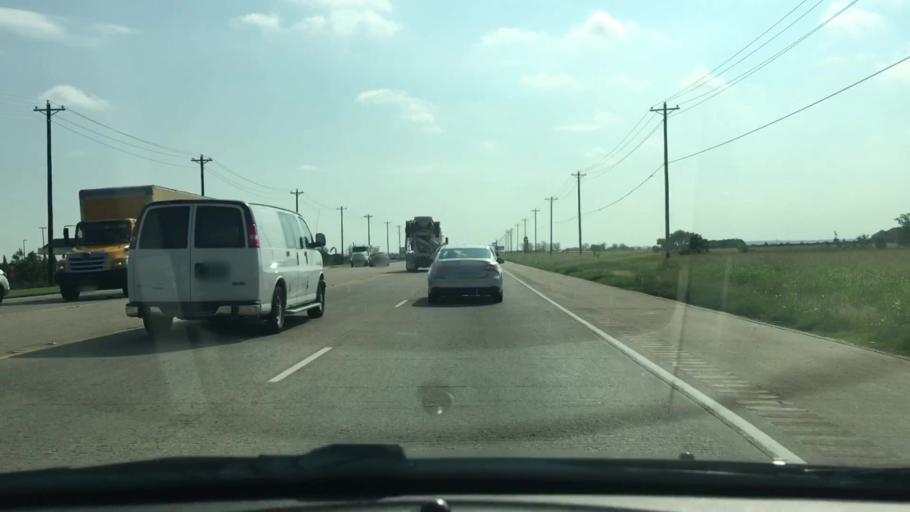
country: US
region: Texas
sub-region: Collin County
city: Prosper
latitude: 33.2189
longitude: -96.8779
